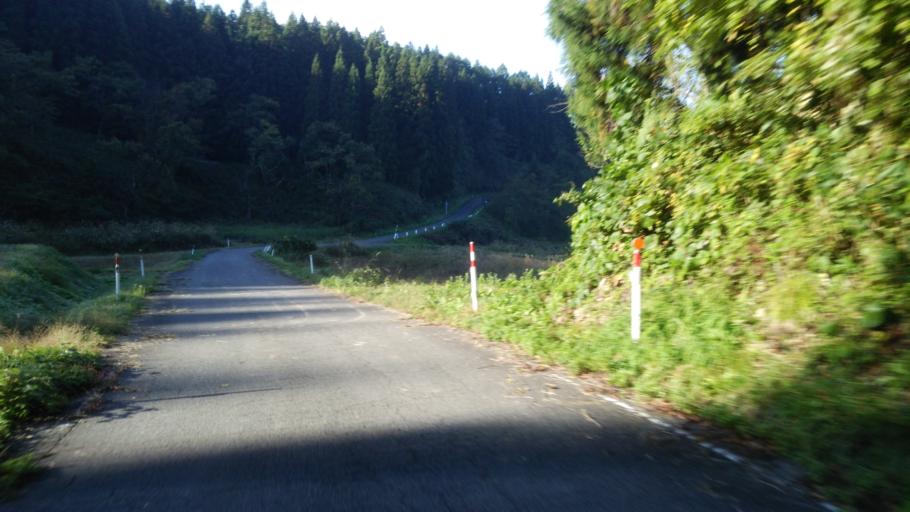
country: JP
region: Fukushima
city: Kitakata
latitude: 37.4479
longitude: 139.7224
